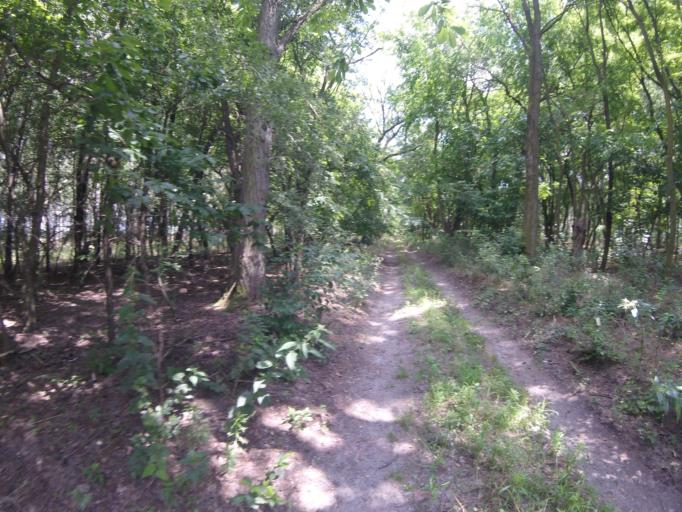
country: HU
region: Pest
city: Nagykoros
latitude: 47.0706
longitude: 19.7537
